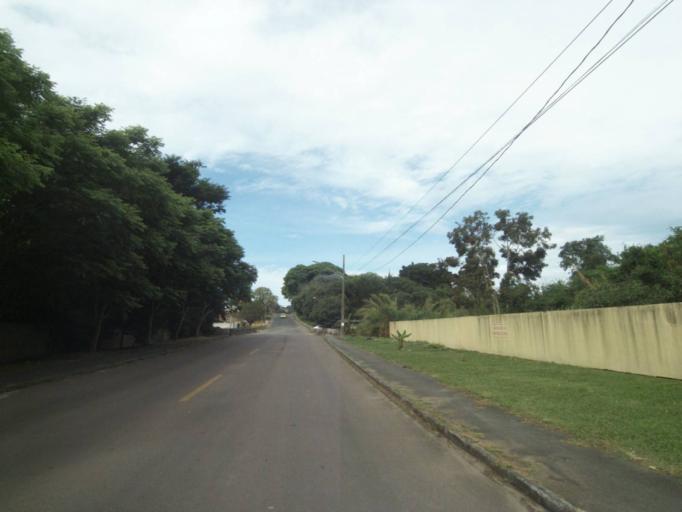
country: BR
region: Parana
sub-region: Pinhais
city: Pinhais
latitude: -25.4201
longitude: -49.2134
